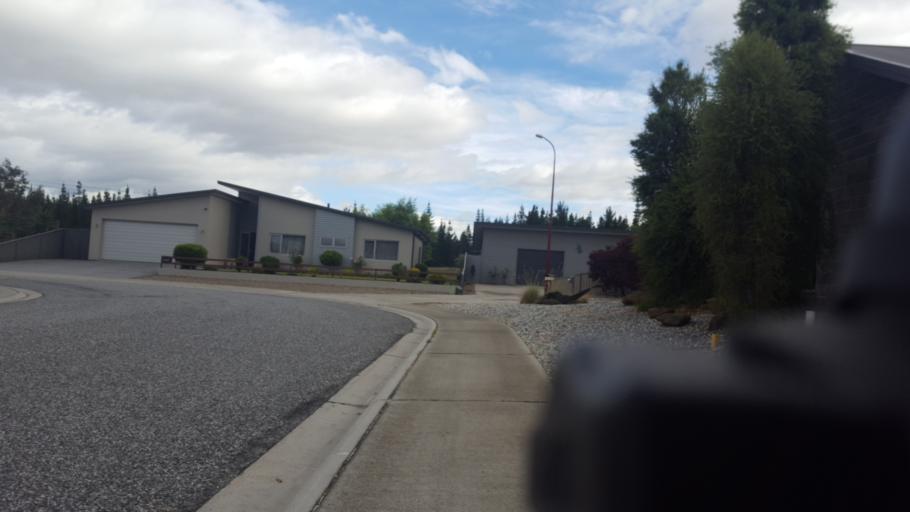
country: NZ
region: Otago
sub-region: Queenstown-Lakes District
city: Wanaka
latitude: -45.2386
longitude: 169.3811
